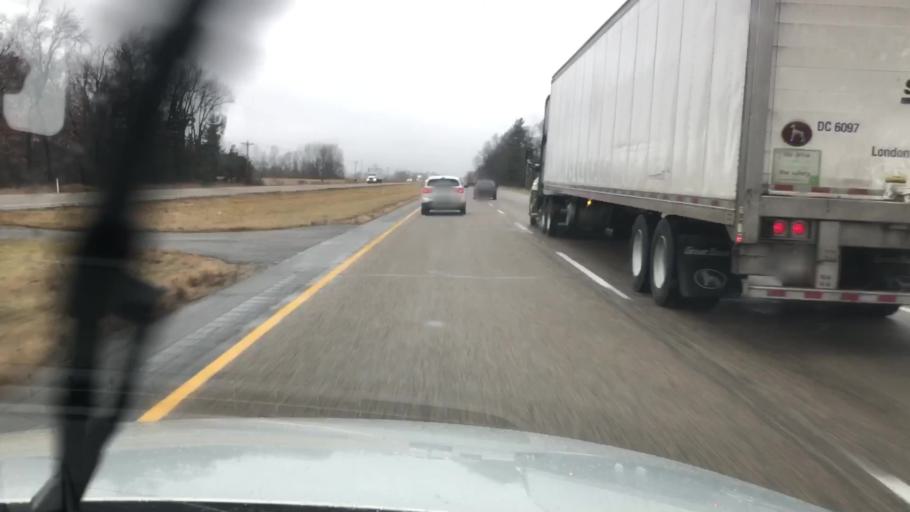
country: US
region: Indiana
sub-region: LaPorte County
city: Wanatah
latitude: 41.4338
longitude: -86.8443
